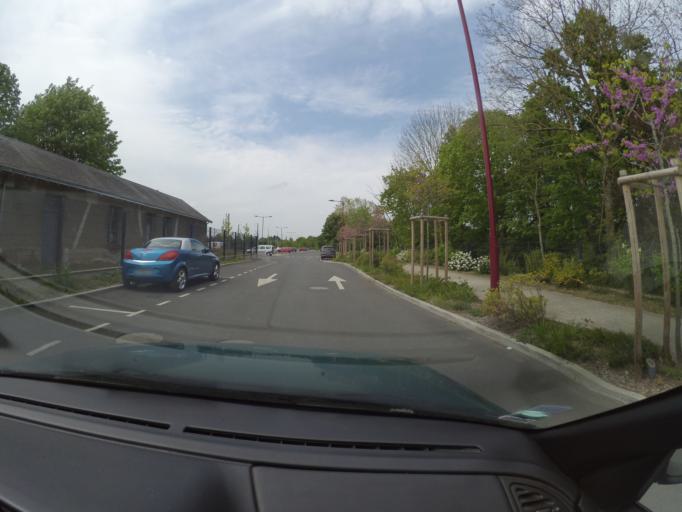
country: FR
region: Pays de la Loire
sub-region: Departement de la Loire-Atlantique
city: Clisson
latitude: 47.0872
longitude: -1.2877
